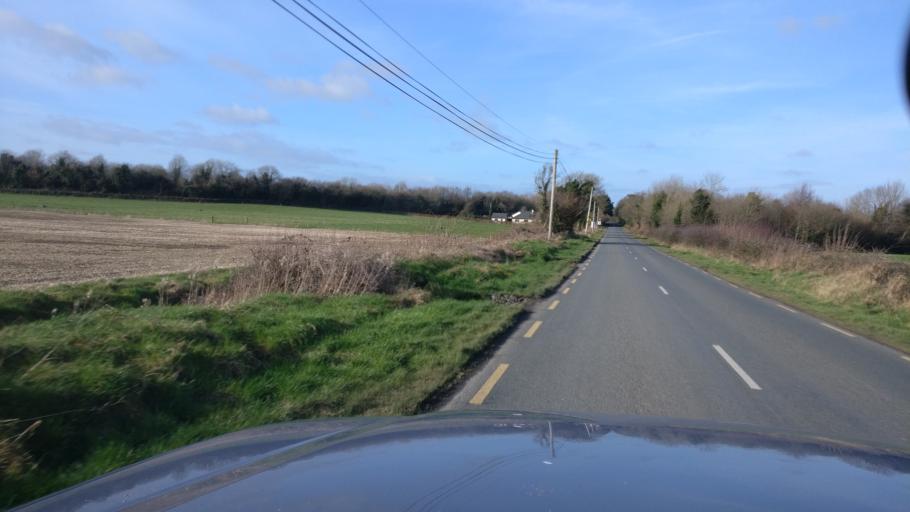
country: IE
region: Leinster
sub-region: Laois
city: Stradbally
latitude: 52.9641
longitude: -7.2042
